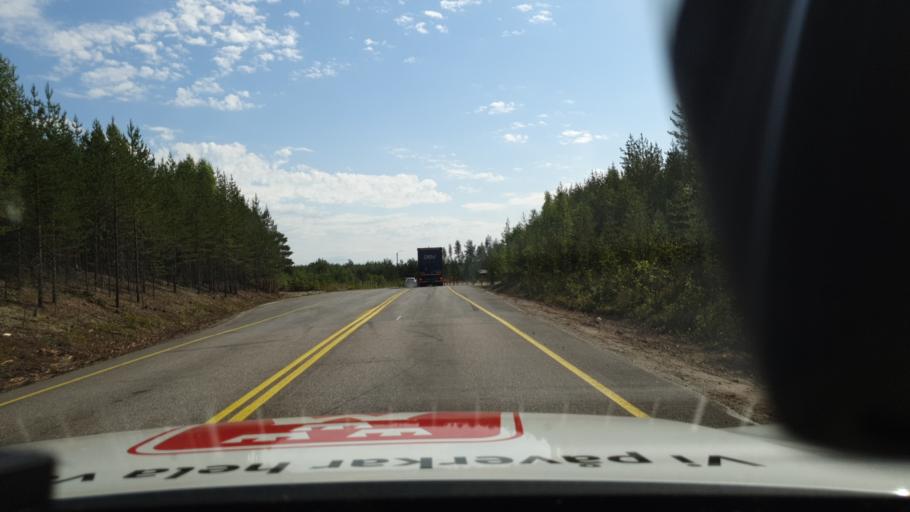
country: SE
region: Norrbotten
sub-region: Lulea Kommun
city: Ranea
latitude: 65.8717
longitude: 22.3564
